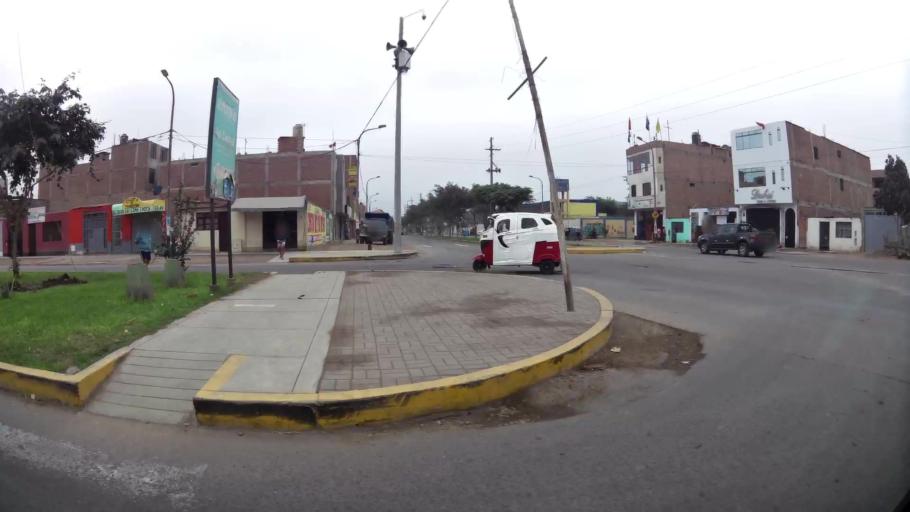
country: PE
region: Lima
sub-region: Lima
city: Independencia
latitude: -11.9620
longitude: -77.0813
